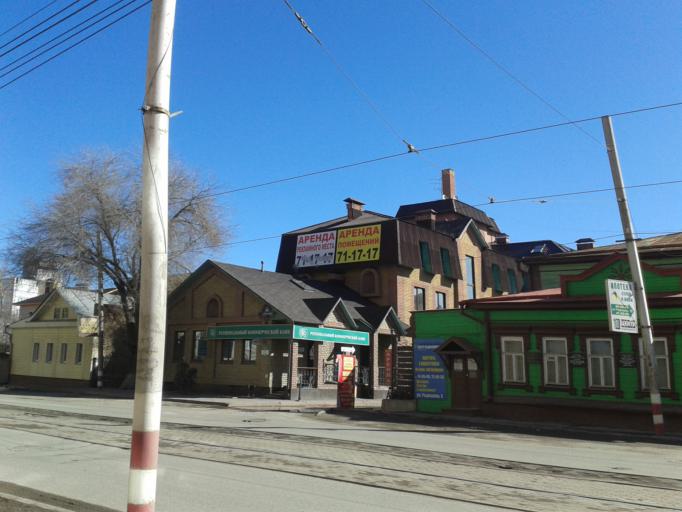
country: RU
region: Ulyanovsk
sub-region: Ulyanovskiy Rayon
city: Ulyanovsk
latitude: 54.3239
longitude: 48.4045
